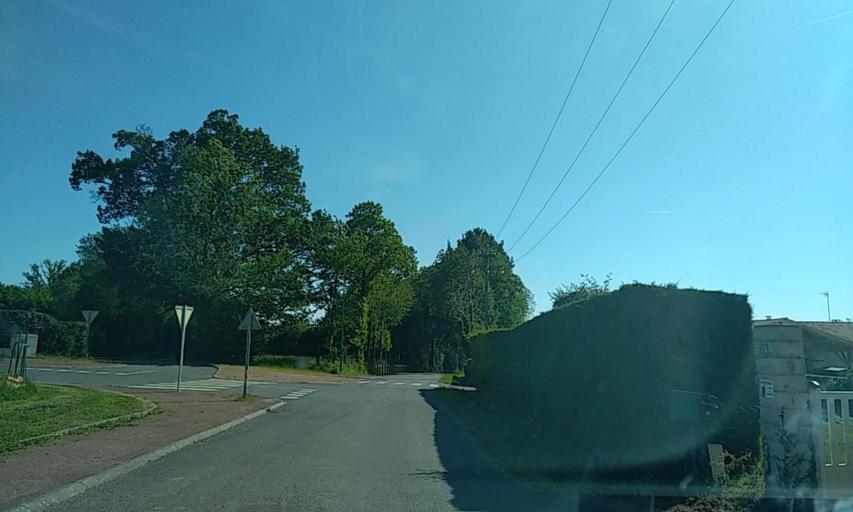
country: FR
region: Poitou-Charentes
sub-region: Departement des Deux-Sevres
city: Boisme
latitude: 46.7791
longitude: -0.4280
